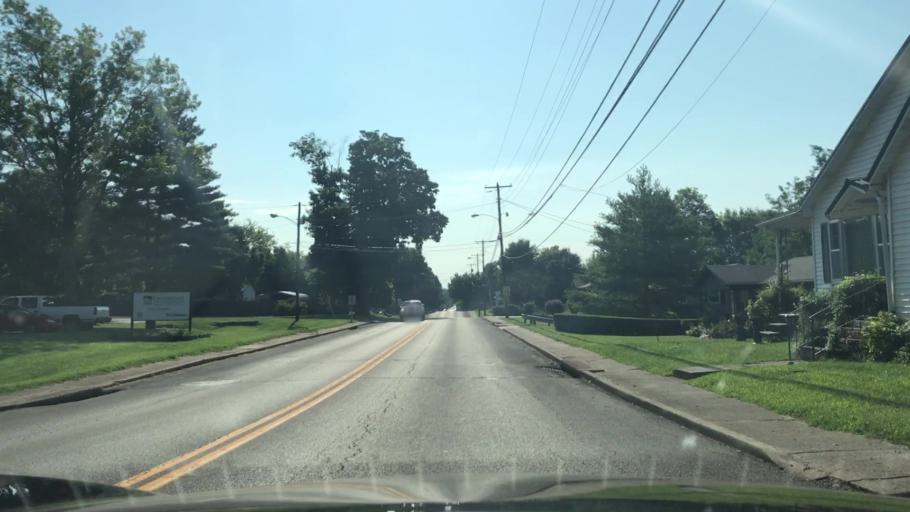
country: US
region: Kentucky
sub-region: Hart County
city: Horse Cave
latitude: 37.1800
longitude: -85.9136
